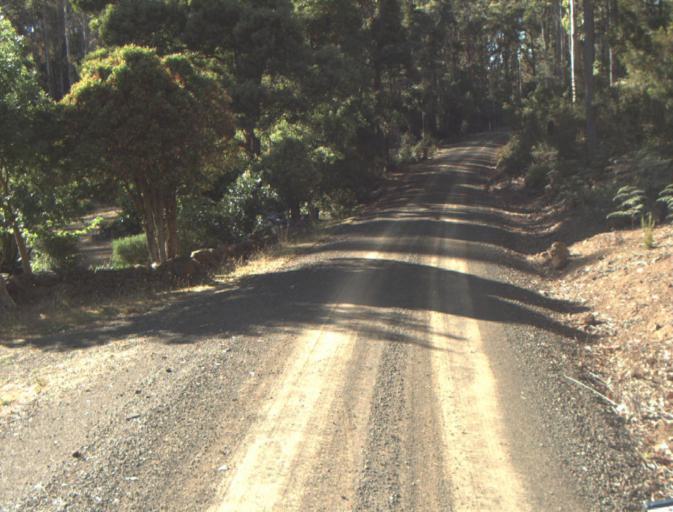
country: AU
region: Tasmania
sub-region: Launceston
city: Mayfield
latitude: -41.2920
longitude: 147.1829
